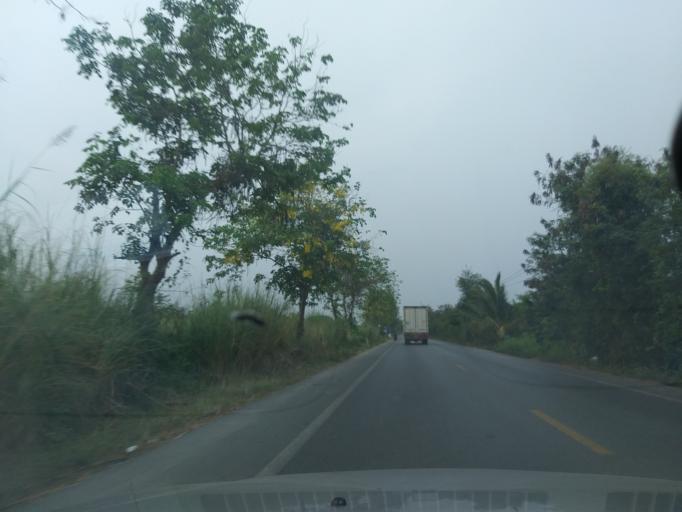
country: TH
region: Pathum Thani
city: Ban Lam Luk Ka
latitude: 14.0040
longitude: 100.8947
